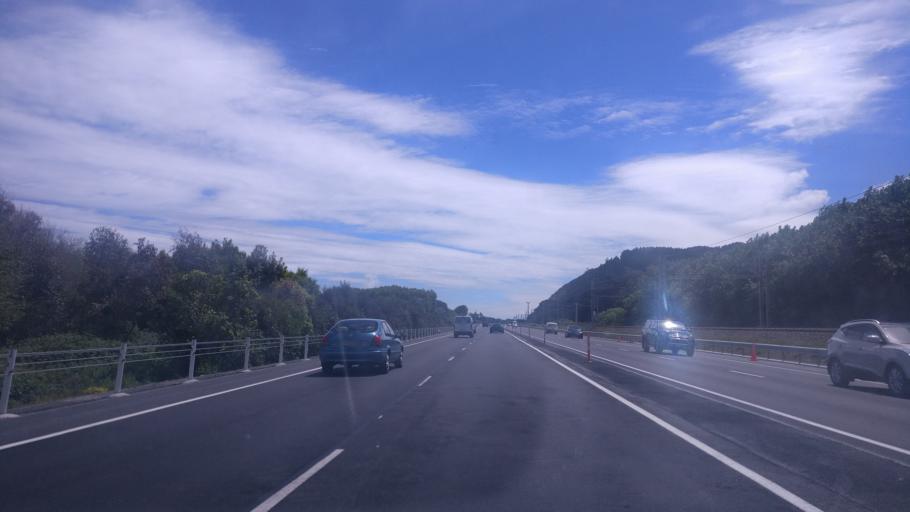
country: NZ
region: Wellington
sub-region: Kapiti Coast District
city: Paraparaumu
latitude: -40.9593
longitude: 174.9876
